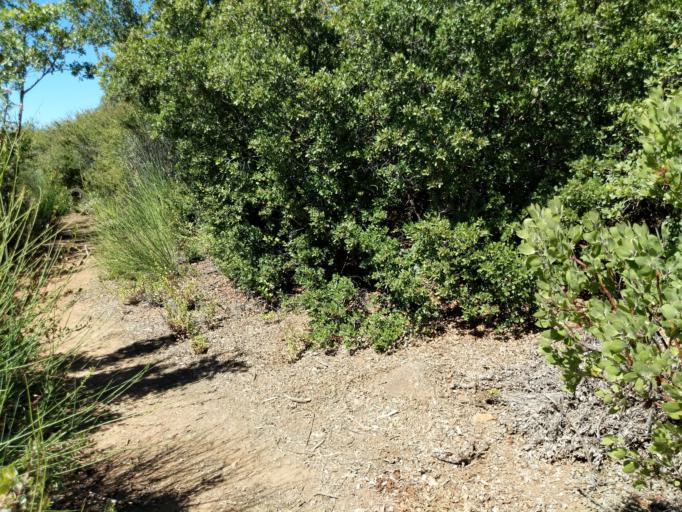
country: US
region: California
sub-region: San Diego County
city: Julian
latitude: 33.0390
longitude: -116.6304
